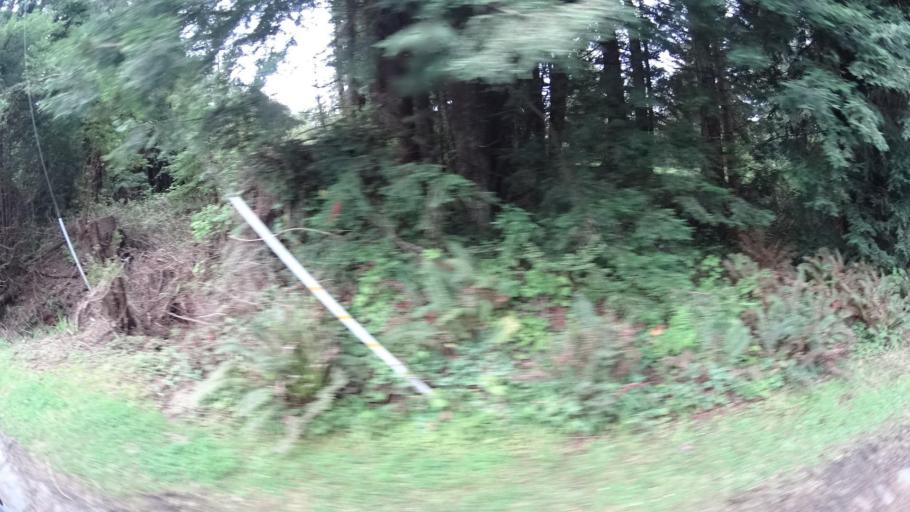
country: US
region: California
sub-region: Humboldt County
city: Blue Lake
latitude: 40.8796
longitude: -123.9809
